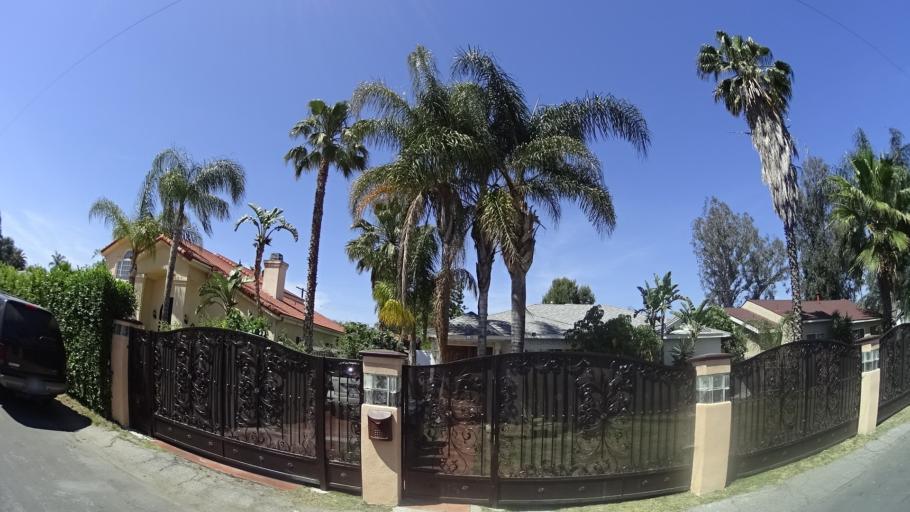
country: US
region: California
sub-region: Los Angeles County
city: North Hollywood
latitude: 34.1744
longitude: -118.3980
